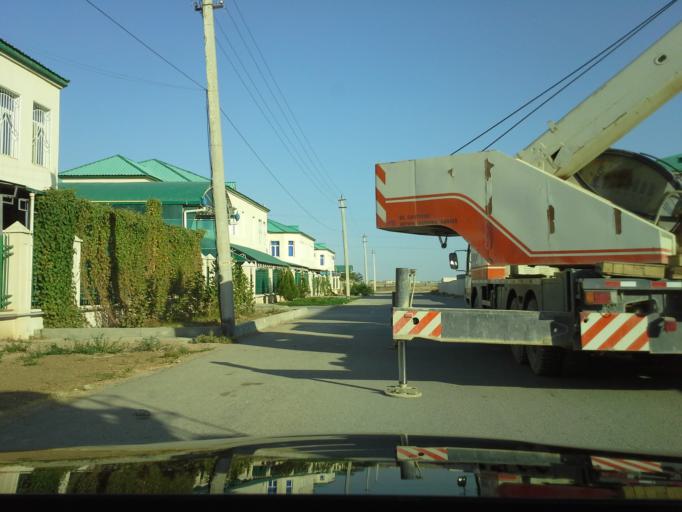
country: TM
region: Ahal
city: Abadan
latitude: 38.0473
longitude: 58.1699
